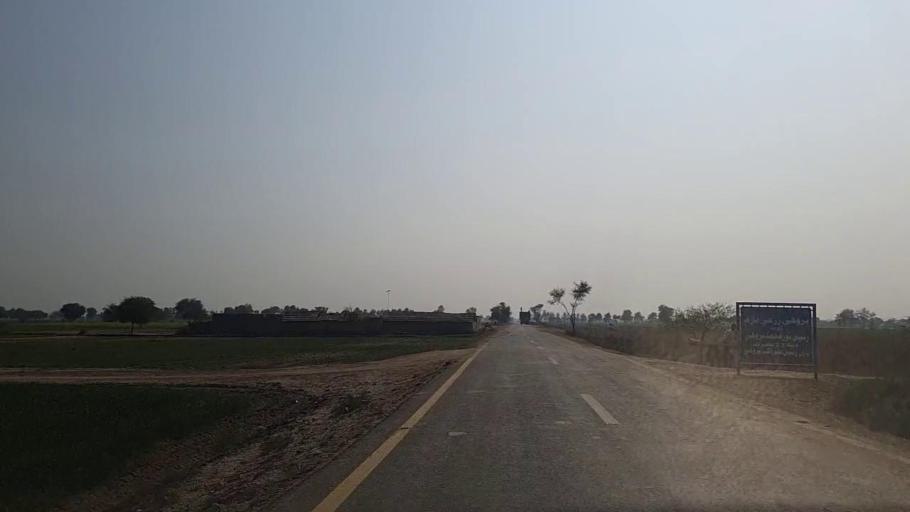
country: PK
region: Sindh
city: Jam Sahib
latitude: 26.3633
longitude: 68.5347
